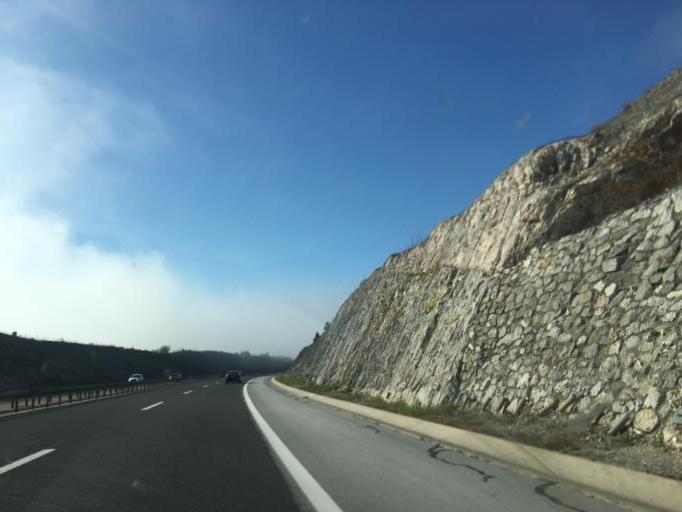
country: HR
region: Licko-Senjska
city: Brinje
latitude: 45.0420
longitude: 15.1777
